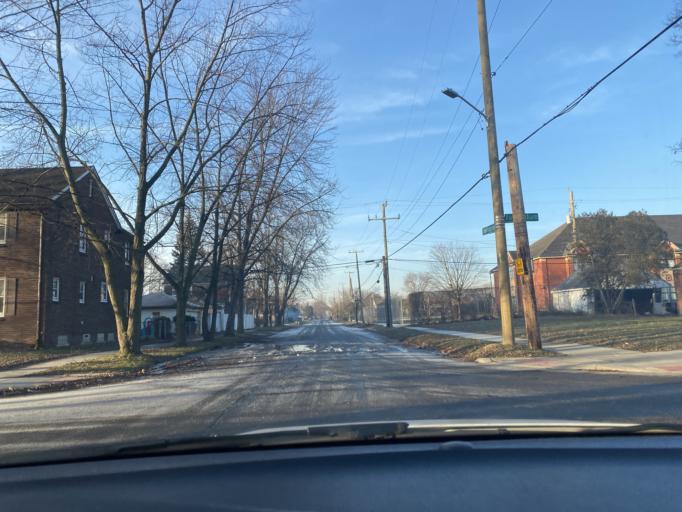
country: US
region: Michigan
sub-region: Wayne County
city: Grosse Pointe Park
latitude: 42.4043
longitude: -82.9459
